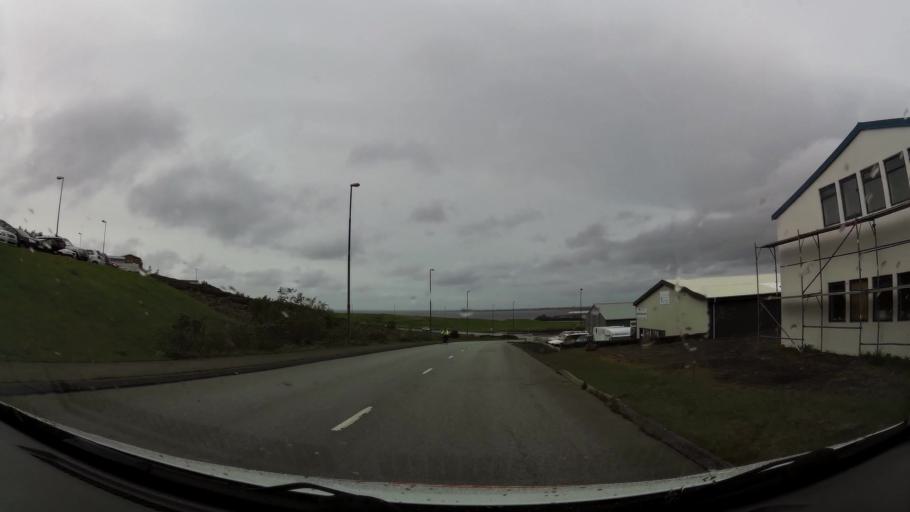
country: IS
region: Capital Region
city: Hafnarfjoerdur
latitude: 64.0583
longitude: -21.9813
